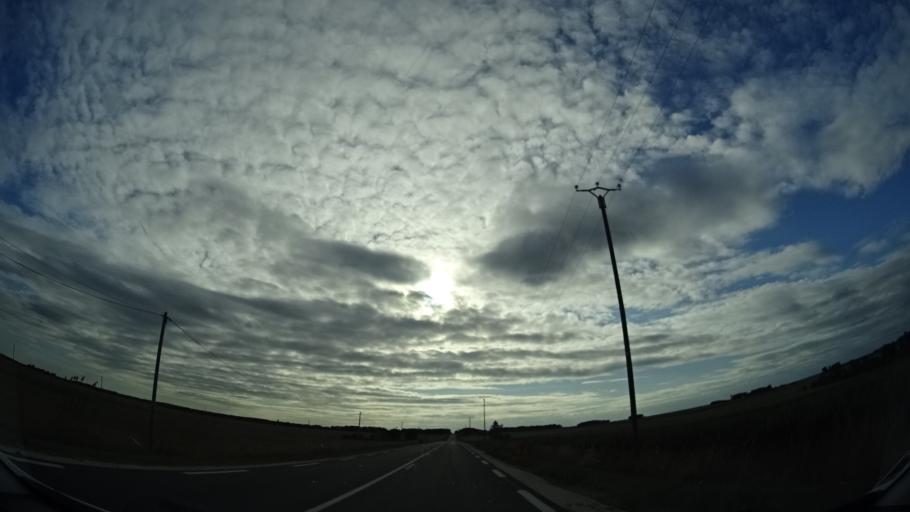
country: FR
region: Centre
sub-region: Departement du Loir-et-Cher
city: La Ville-aux-Clercs
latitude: 47.8926
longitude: 1.0935
